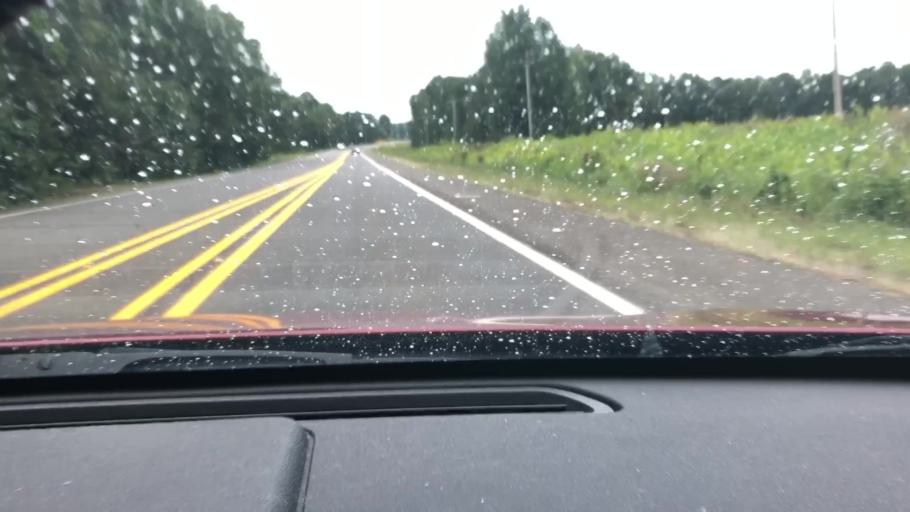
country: US
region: Arkansas
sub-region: Columbia County
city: Waldo
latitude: 33.3508
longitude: -93.3619
